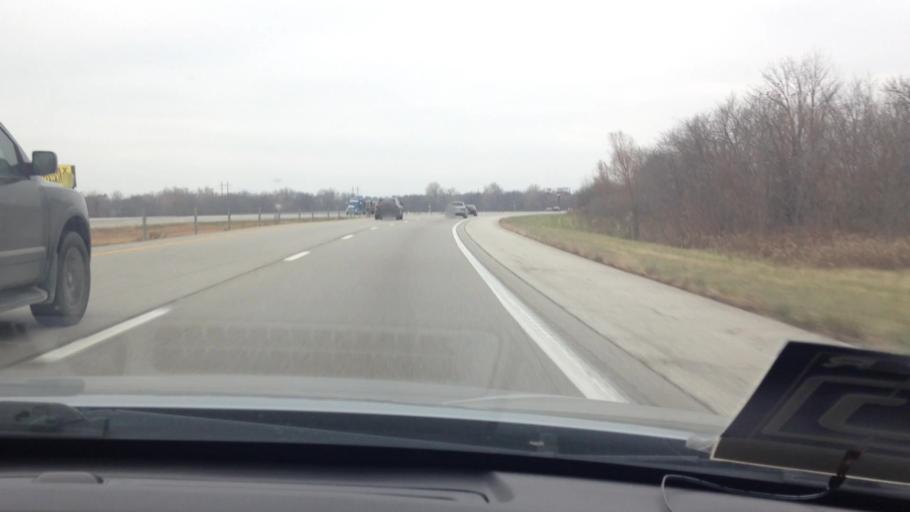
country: US
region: Missouri
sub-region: Cass County
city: Raymore
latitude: 38.7632
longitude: -94.4894
